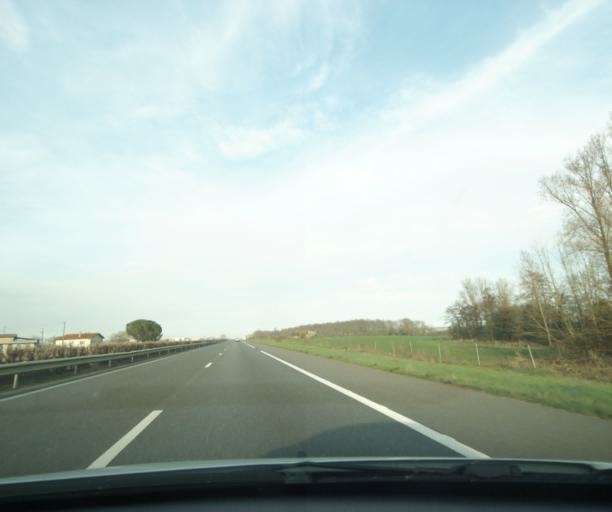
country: FR
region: Midi-Pyrenees
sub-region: Departement de la Haute-Garonne
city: Le Fousseret
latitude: 43.2650
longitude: 1.1235
